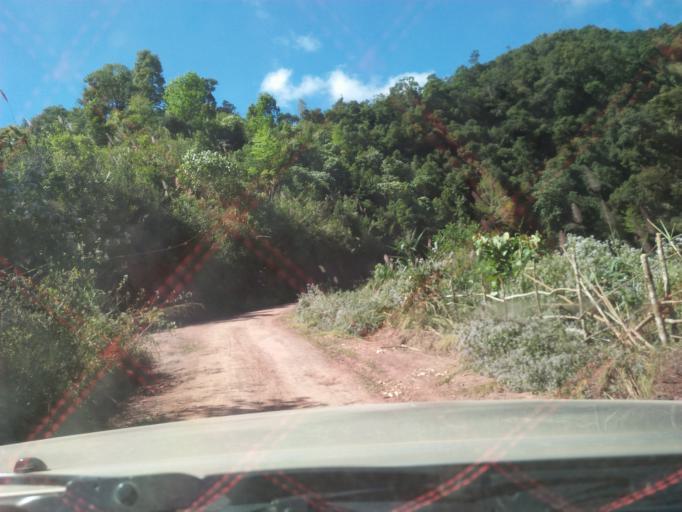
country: TH
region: Nan
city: Chaloem Phra Kiat
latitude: 19.4568
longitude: 101.2739
